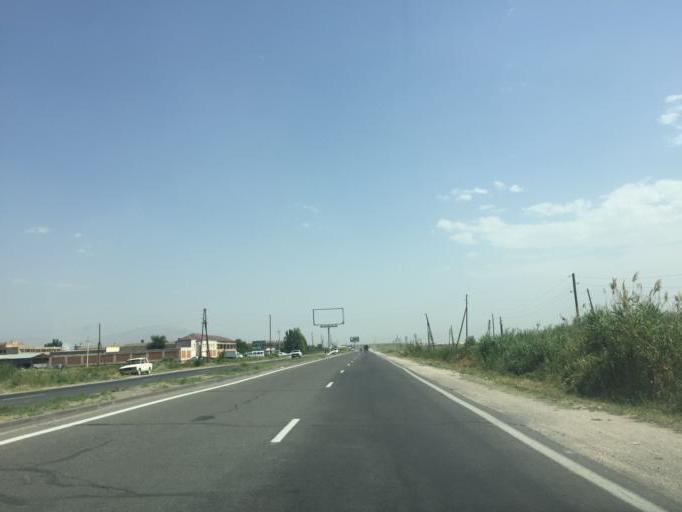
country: AM
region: Ararat
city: Shahumyan
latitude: 39.9400
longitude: 44.5569
